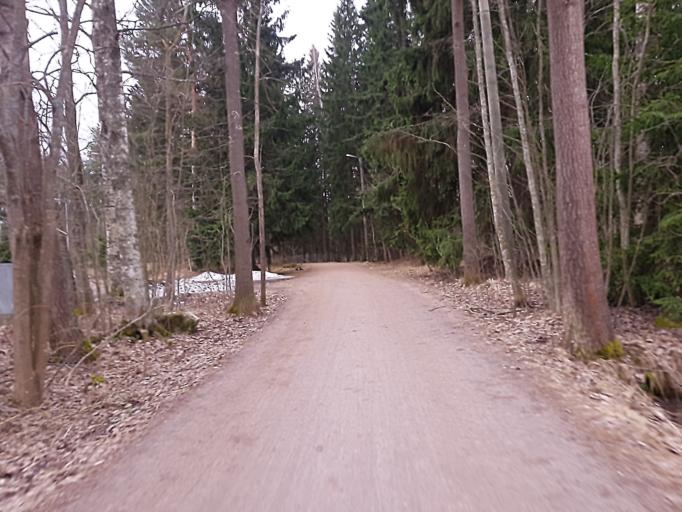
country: FI
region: Uusimaa
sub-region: Helsinki
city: Helsinki
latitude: 60.2409
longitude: 24.9126
